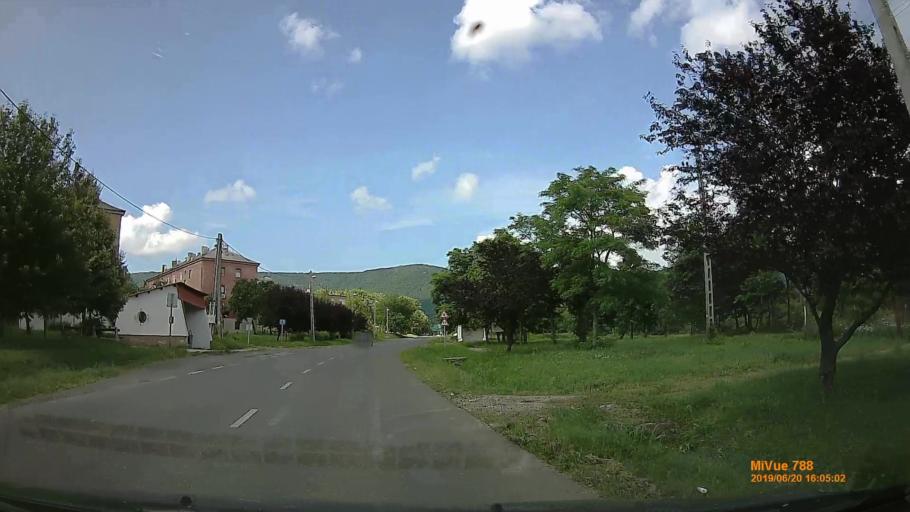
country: HU
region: Baranya
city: Pellerd
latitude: 46.0767
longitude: 18.1168
